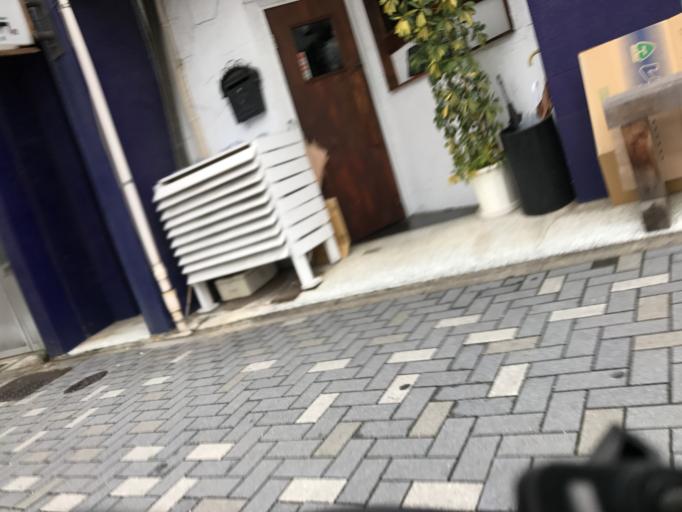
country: JP
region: Aichi
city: Nagoya-shi
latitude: 35.1683
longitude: 136.9210
